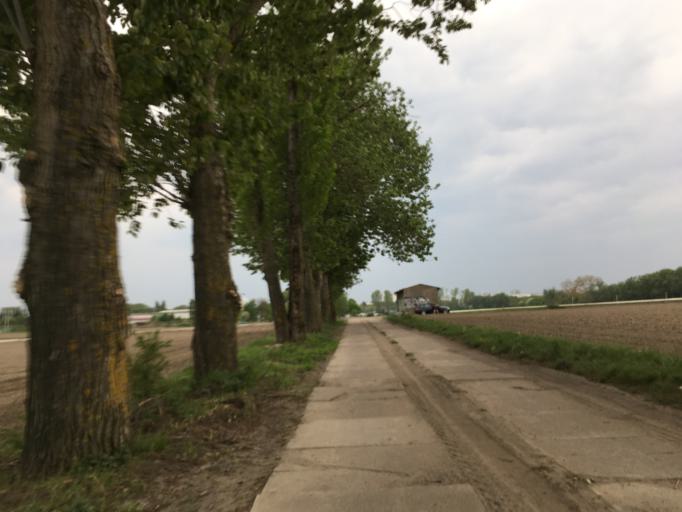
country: DE
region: Berlin
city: Wartenberg
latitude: 52.5851
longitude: 13.5190
